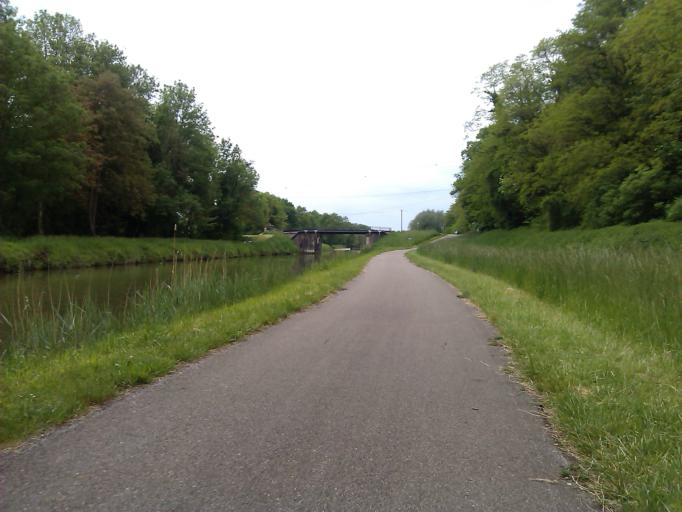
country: FR
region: Franche-Comte
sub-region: Departement du Jura
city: Choisey
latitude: 47.0738
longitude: 5.4710
